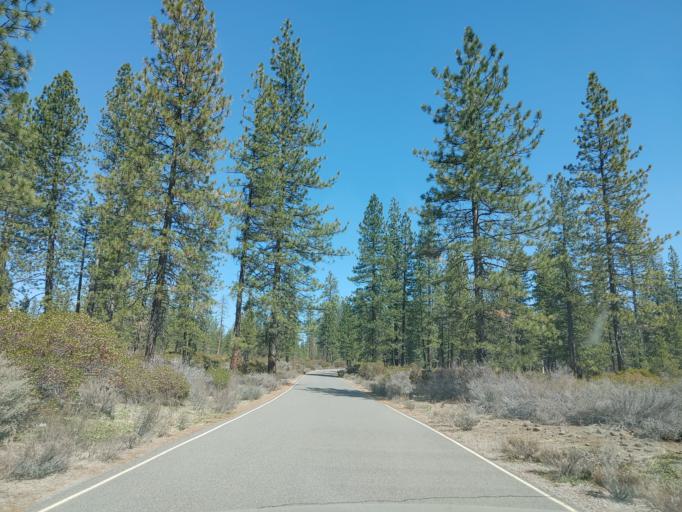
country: US
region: California
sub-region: Siskiyou County
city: McCloud
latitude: 41.2456
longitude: -122.0282
